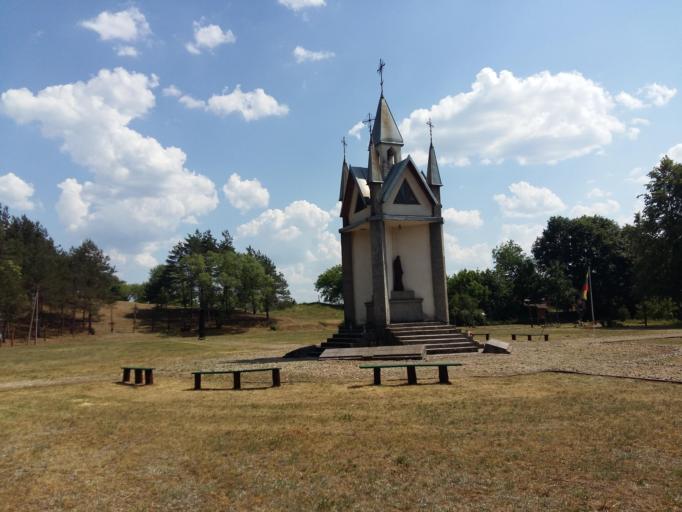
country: LT
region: Alytaus apskritis
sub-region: Alytaus rajonas
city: Daugai
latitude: 54.1654
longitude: 24.1823
